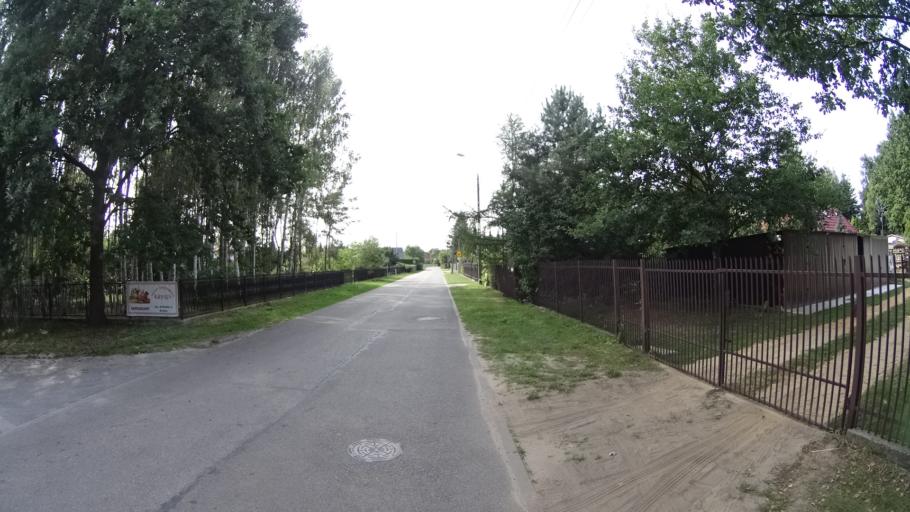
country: PL
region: Masovian Voivodeship
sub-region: Powiat legionowski
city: Serock
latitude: 52.4753
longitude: 21.0883
